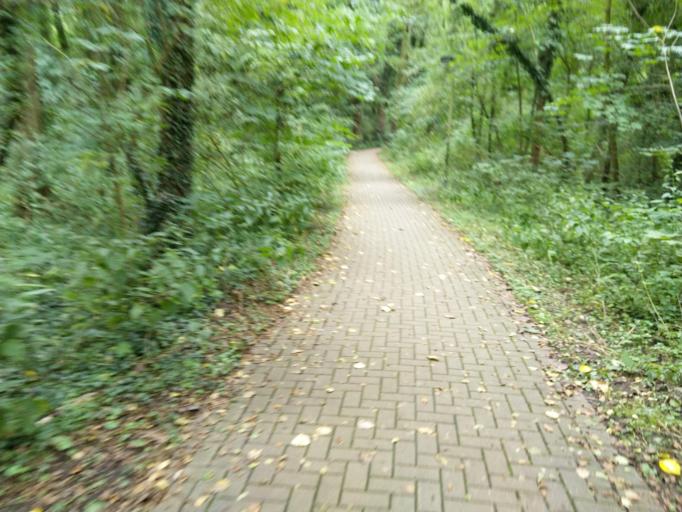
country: DE
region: North Rhine-Westphalia
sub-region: Regierungsbezirk Detmold
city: Bad Salzuflen
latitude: 52.0980
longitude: 8.7650
